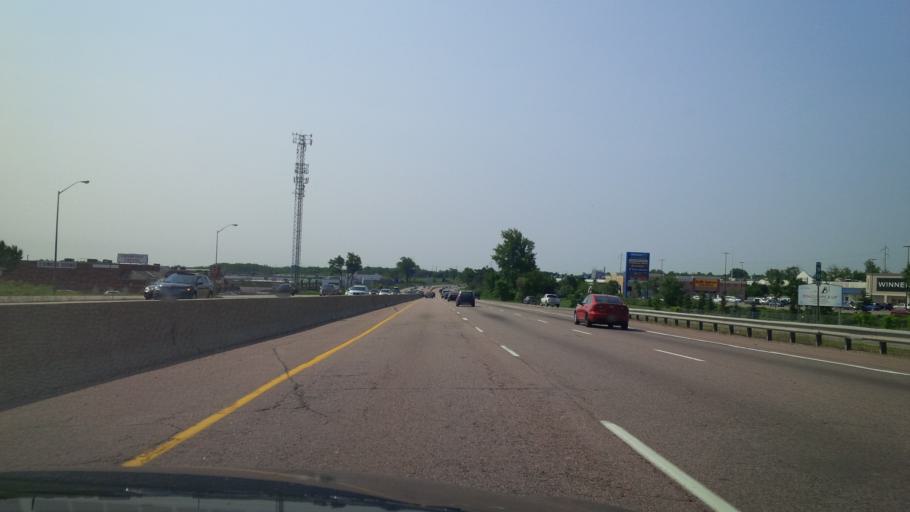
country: CA
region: Ontario
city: Innisfil
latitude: 44.3332
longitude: -79.6842
